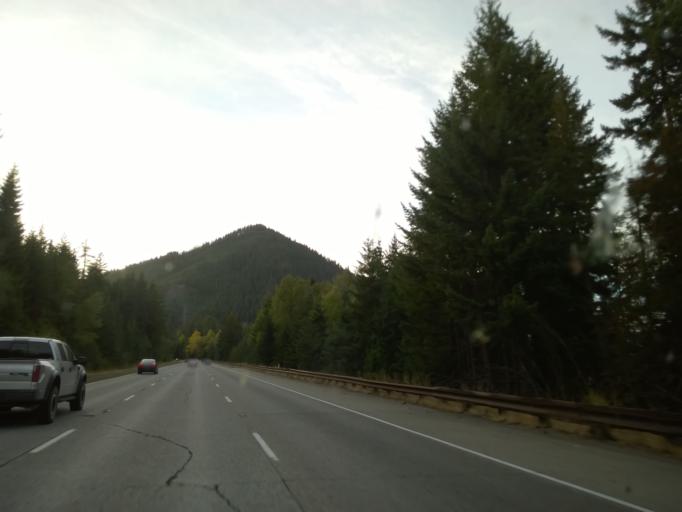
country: US
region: Washington
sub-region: Kittitas County
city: Cle Elum
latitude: 47.2677
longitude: -121.2268
